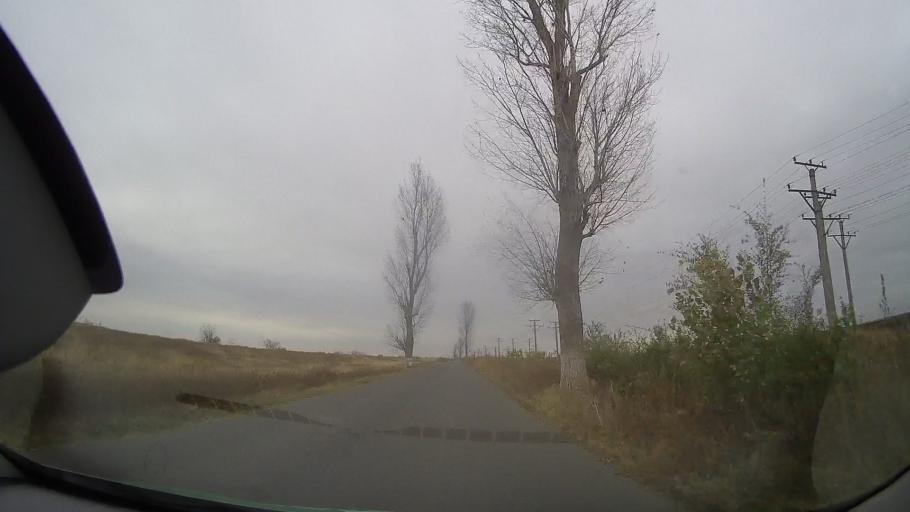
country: RO
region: Braila
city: Dudesti
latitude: 44.9007
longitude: 27.4324
